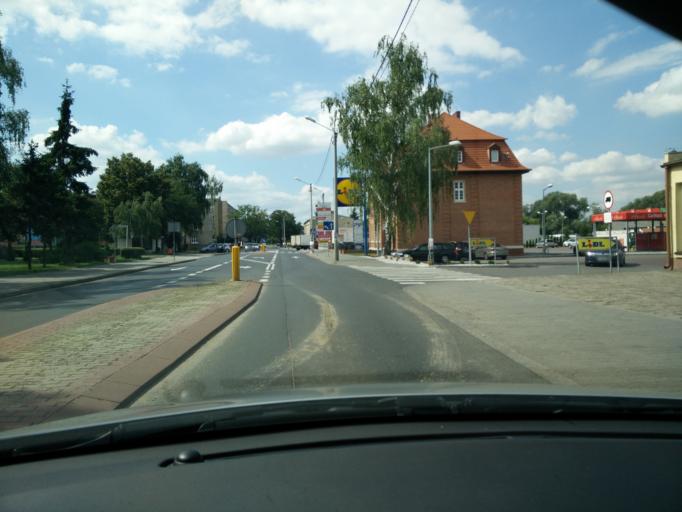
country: PL
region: Greater Poland Voivodeship
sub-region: Powiat sredzki
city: Sroda Wielkopolska
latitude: 52.2307
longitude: 17.2699
